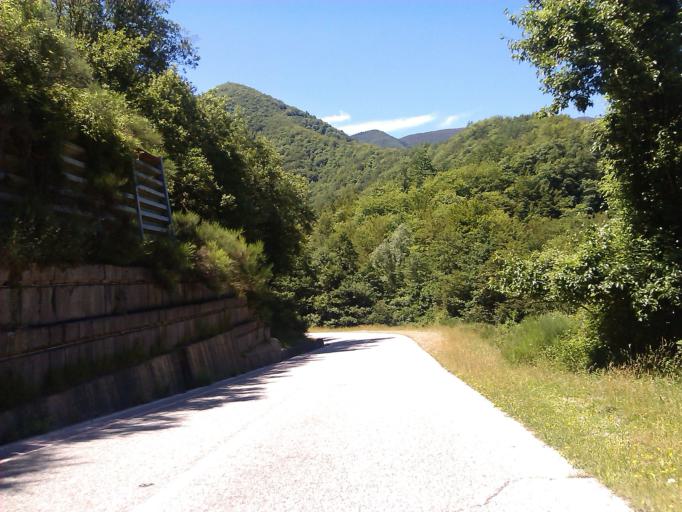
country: IT
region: Tuscany
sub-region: Provincia di Prato
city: Cantagallo
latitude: 44.0431
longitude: 11.0398
